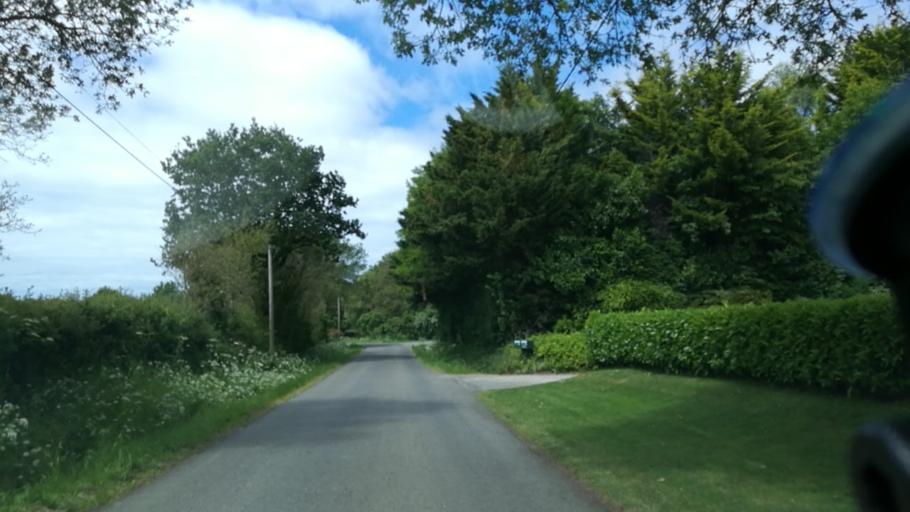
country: FR
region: Pays de la Loire
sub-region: Departement de la Loire-Atlantique
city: Asserac
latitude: 47.4453
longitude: -2.4185
